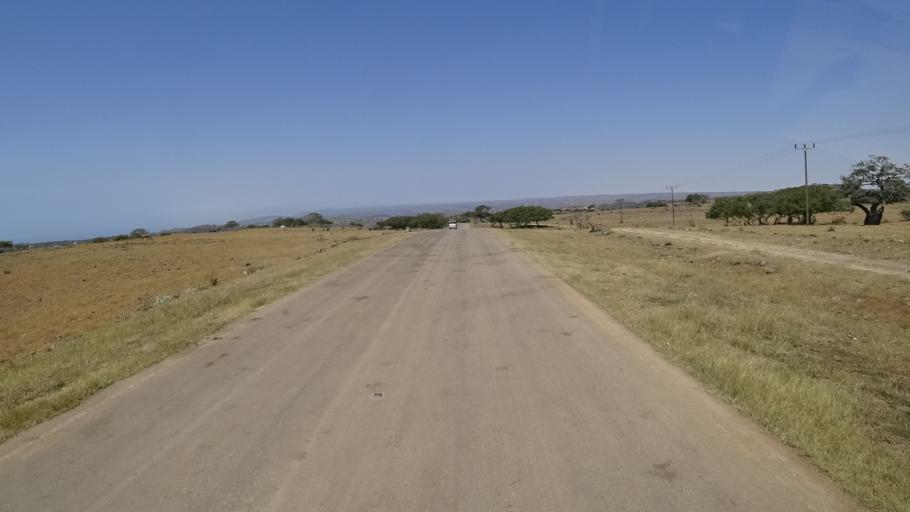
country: OM
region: Zufar
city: Salalah
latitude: 17.1217
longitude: 54.5880
